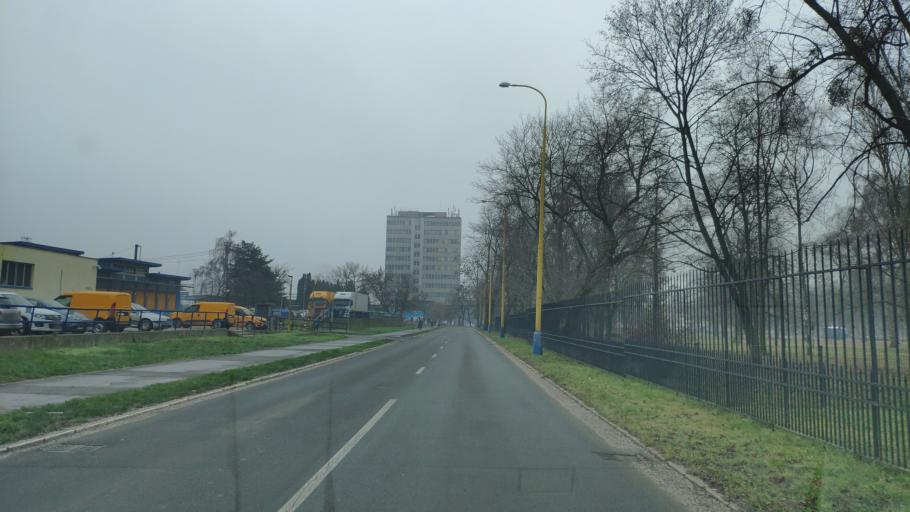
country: SK
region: Kosicky
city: Kosice
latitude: 48.7256
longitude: 21.2660
